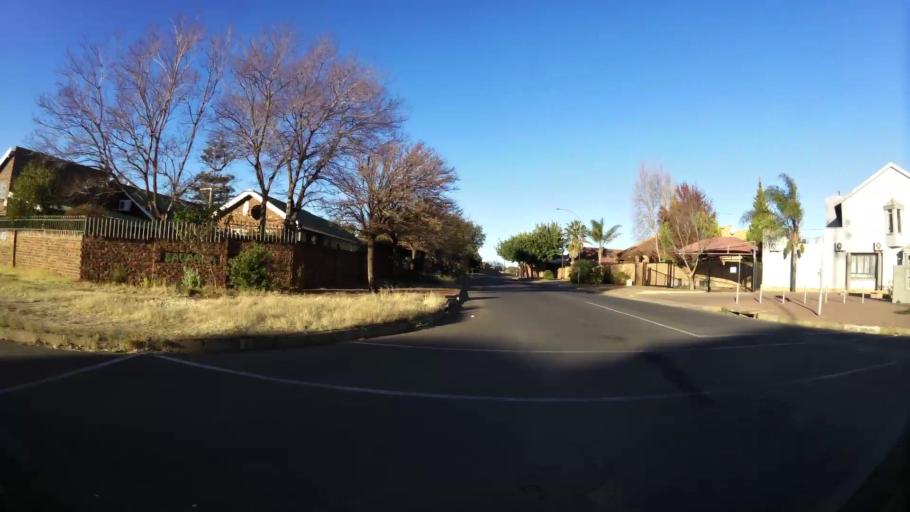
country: ZA
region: Northern Cape
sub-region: Frances Baard District Municipality
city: Kimberley
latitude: -28.7640
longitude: 24.7519
